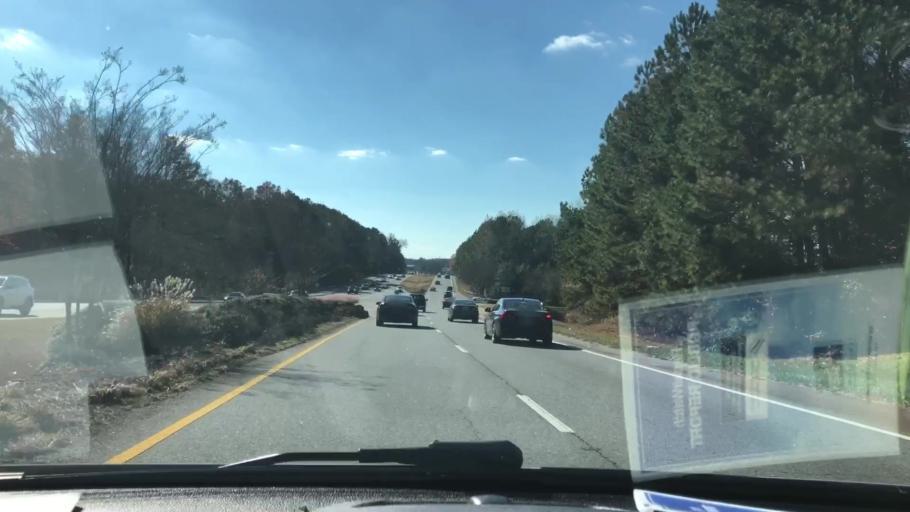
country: US
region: Georgia
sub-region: Gwinnett County
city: Norcross
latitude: 33.9631
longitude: -84.2244
